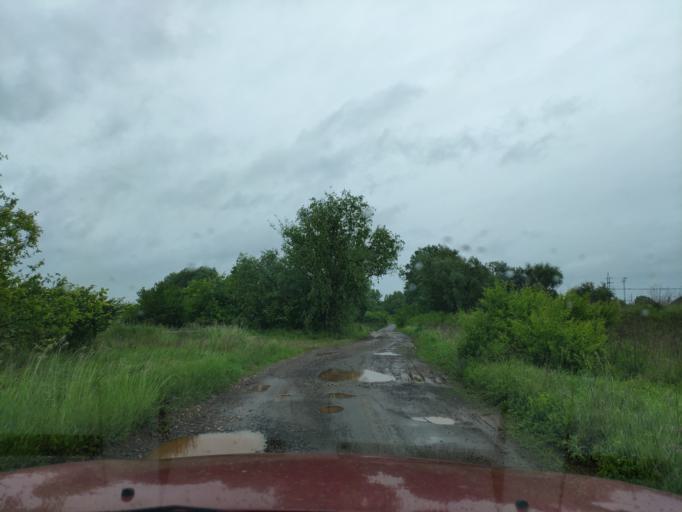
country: SK
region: Kosicky
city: Cierna nad Tisou
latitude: 48.4235
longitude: 22.0806
